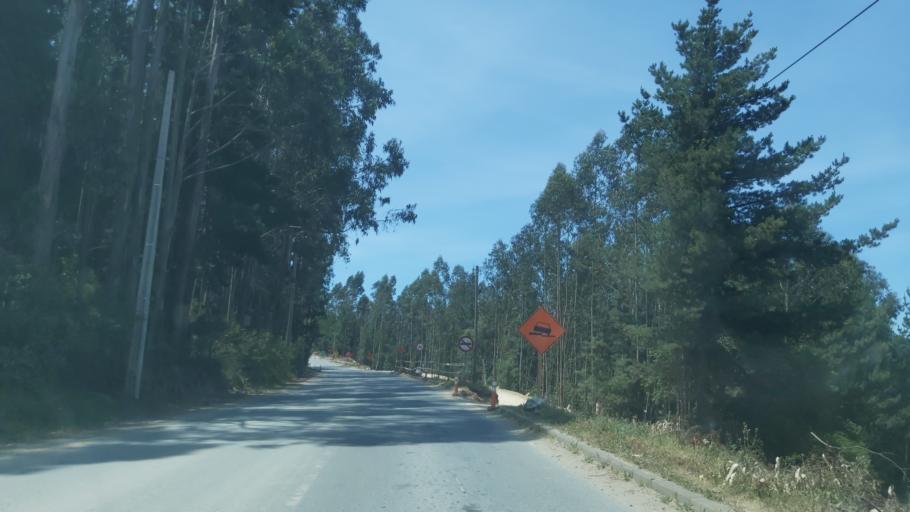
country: CL
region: Maule
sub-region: Provincia de Talca
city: Constitucion
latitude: -35.4407
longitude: -72.4567
